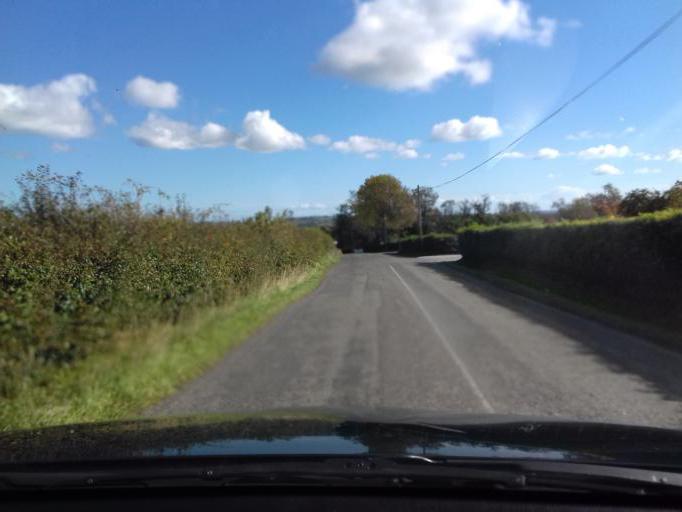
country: IE
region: Leinster
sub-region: An Mhi
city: Slane
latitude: 53.6873
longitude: -6.5221
